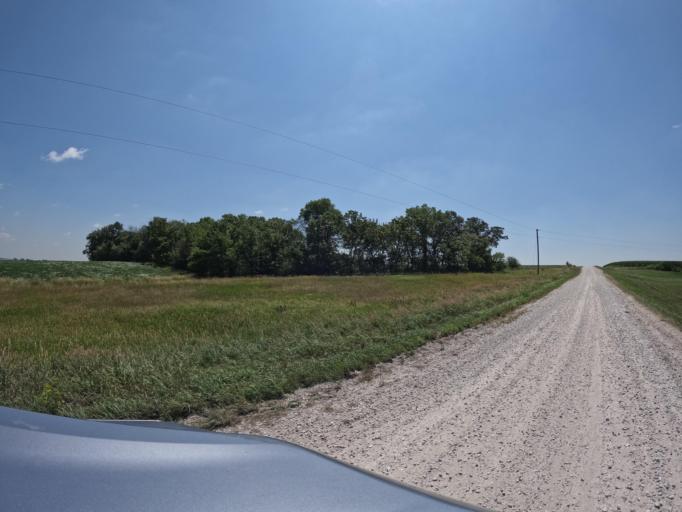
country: US
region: Iowa
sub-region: Keokuk County
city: Sigourney
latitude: 41.2830
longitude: -92.2381
